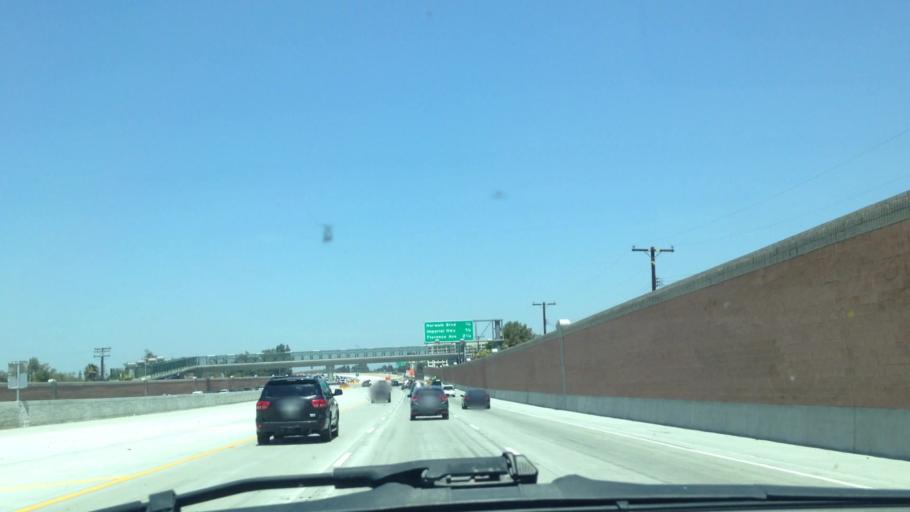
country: US
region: California
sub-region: Los Angeles County
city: Norwalk
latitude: 33.9059
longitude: -118.0657
